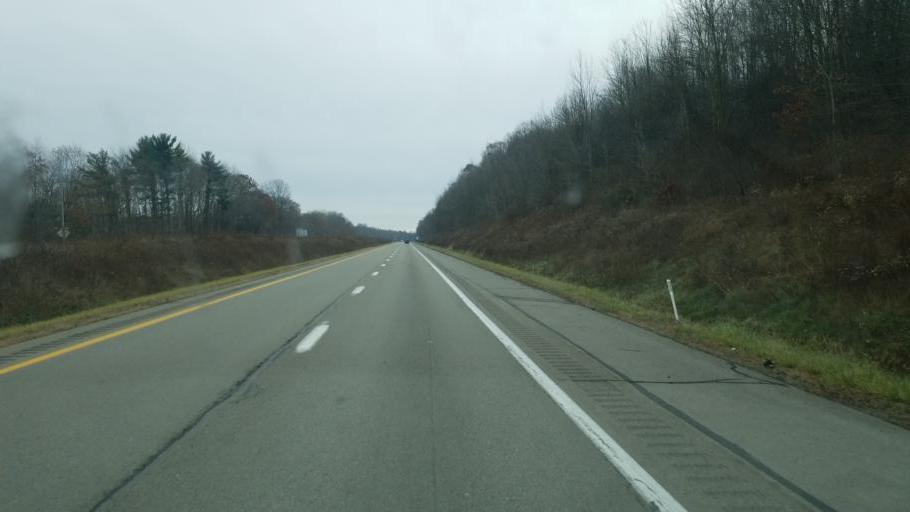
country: US
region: Pennsylvania
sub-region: Crawford County
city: Meadville
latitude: 41.5343
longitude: -80.1798
